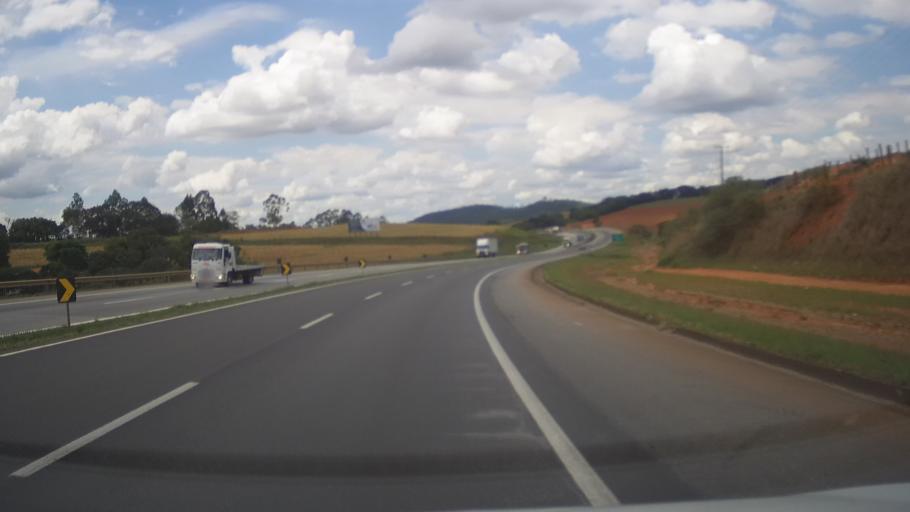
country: BR
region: Minas Gerais
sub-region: Nepomuceno
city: Nepomuceno
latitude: -21.2298
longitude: -45.1337
